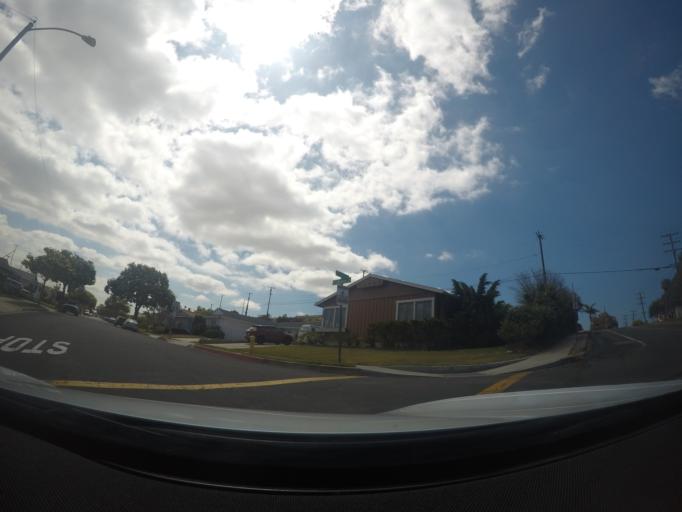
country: US
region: California
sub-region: Los Angeles County
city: Palos Verdes Estates
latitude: 33.8072
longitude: -118.3743
